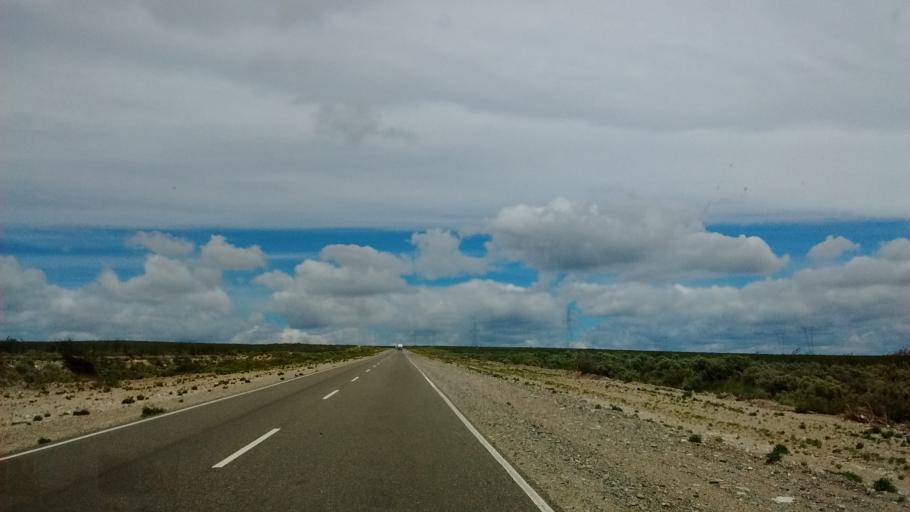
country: AR
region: Neuquen
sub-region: Departamento de Picun Leufu
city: Picun Leufu
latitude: -39.7305
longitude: -69.5758
